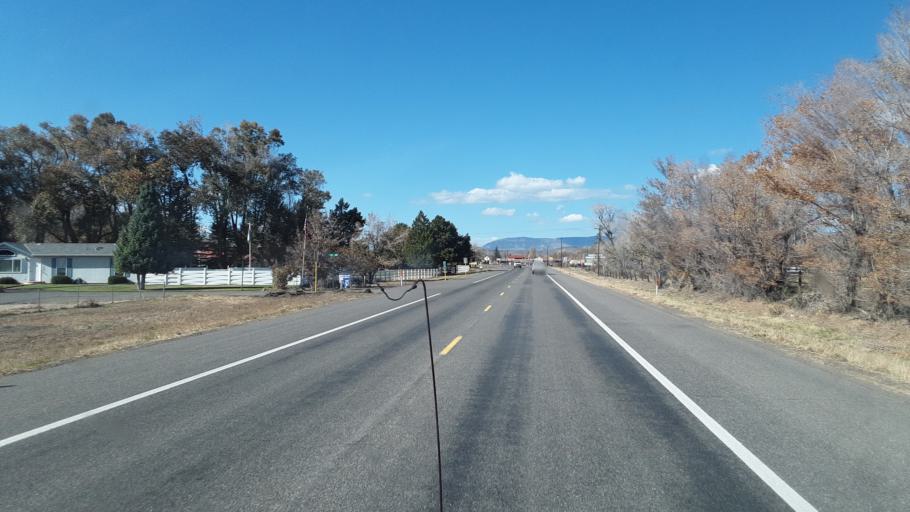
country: US
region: Colorado
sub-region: Rio Grande County
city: Del Norte
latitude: 37.6773
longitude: -106.3382
